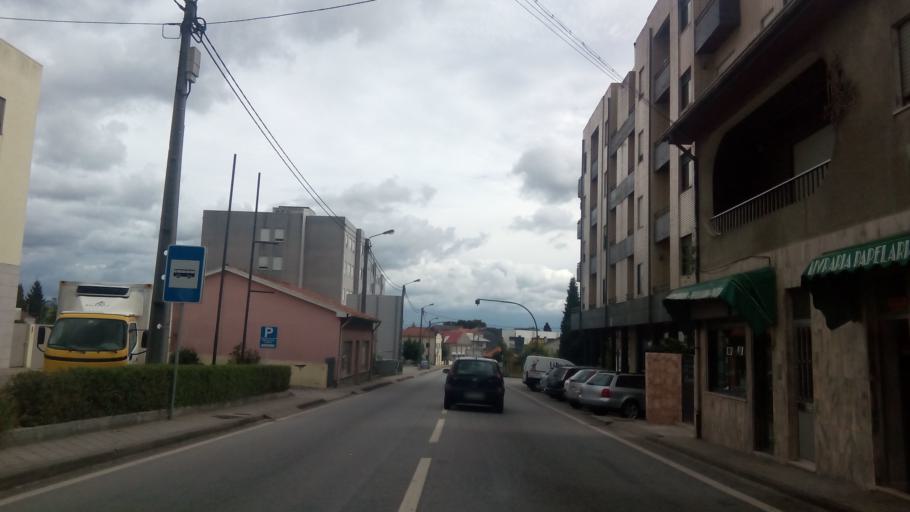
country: PT
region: Porto
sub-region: Paredes
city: Baltar
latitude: 41.1918
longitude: -8.3860
